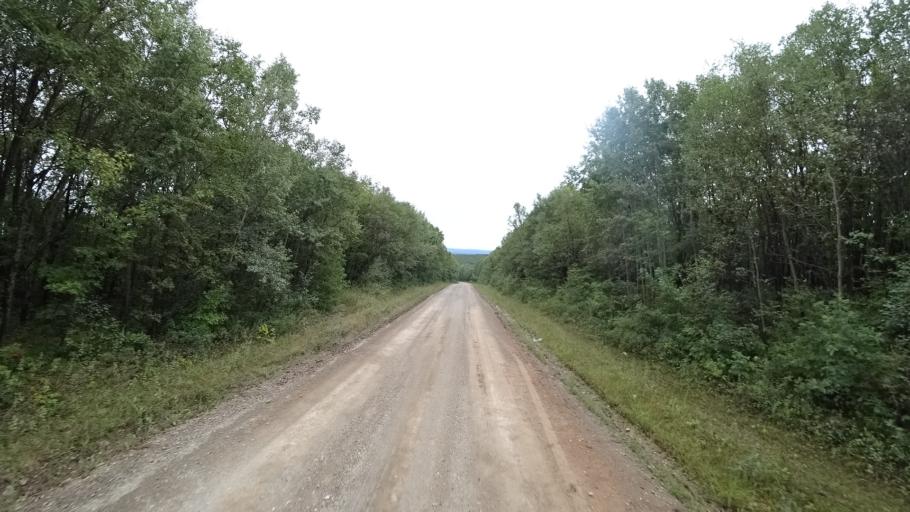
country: RU
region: Primorskiy
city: Ivanovka
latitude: 44.0341
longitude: 132.5031
